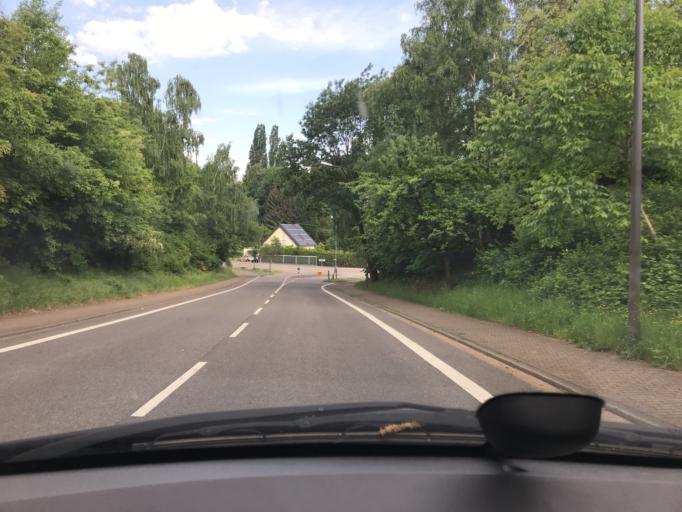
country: DE
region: Saarland
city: Saarlouis
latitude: 49.3306
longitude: 6.7719
